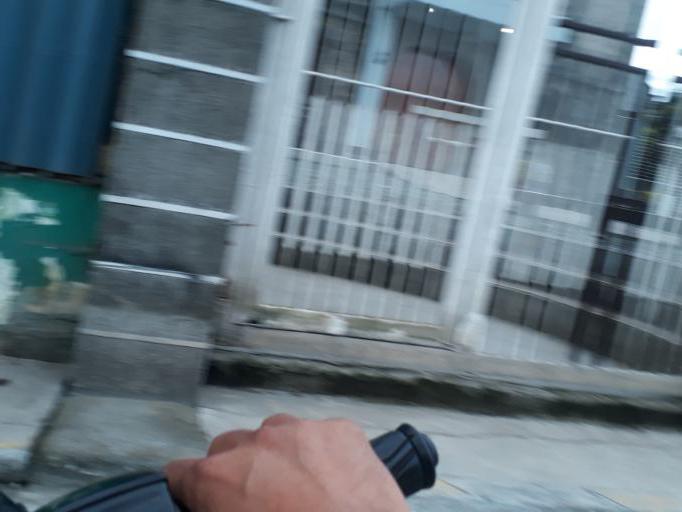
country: PH
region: Central Luzon
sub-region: Province of Bulacan
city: Obando
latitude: 14.7109
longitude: 120.9498
